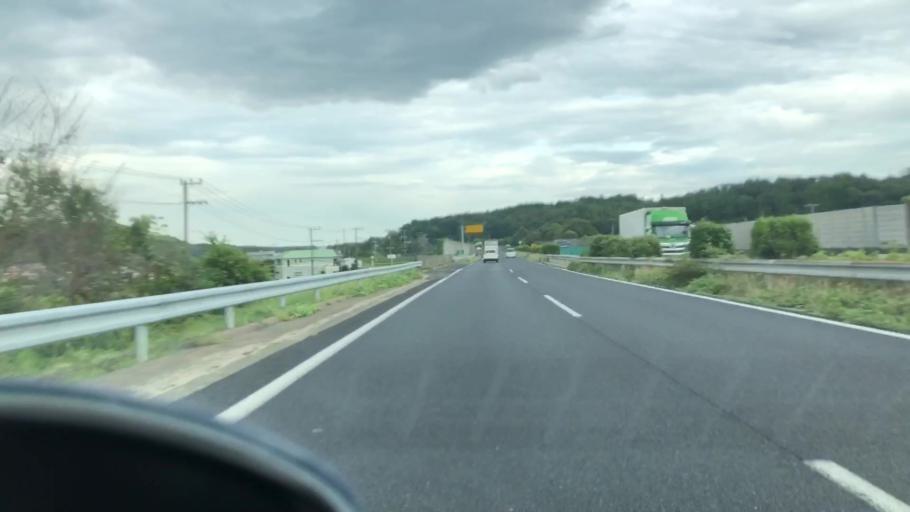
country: JP
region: Hyogo
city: Yashiro
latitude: 34.9194
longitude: 135.0081
